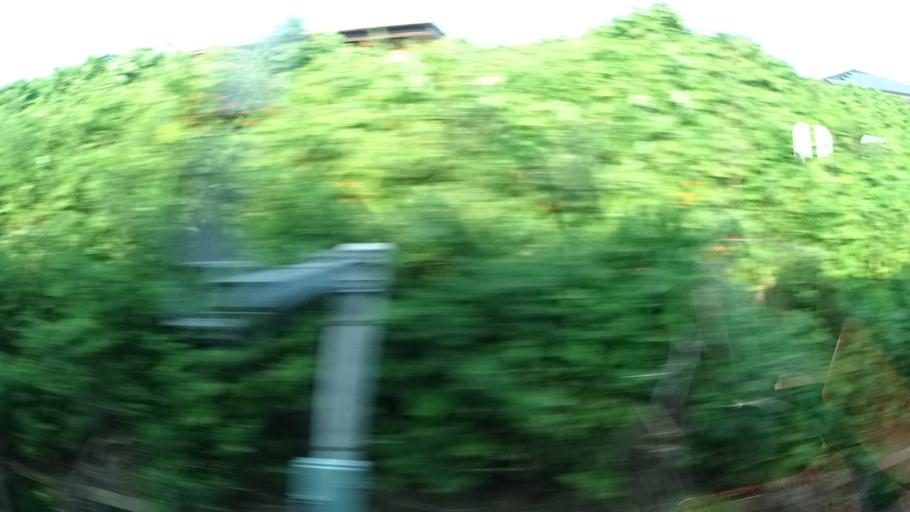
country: JP
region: Ibaraki
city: Hitachi
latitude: 36.6419
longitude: 140.6737
